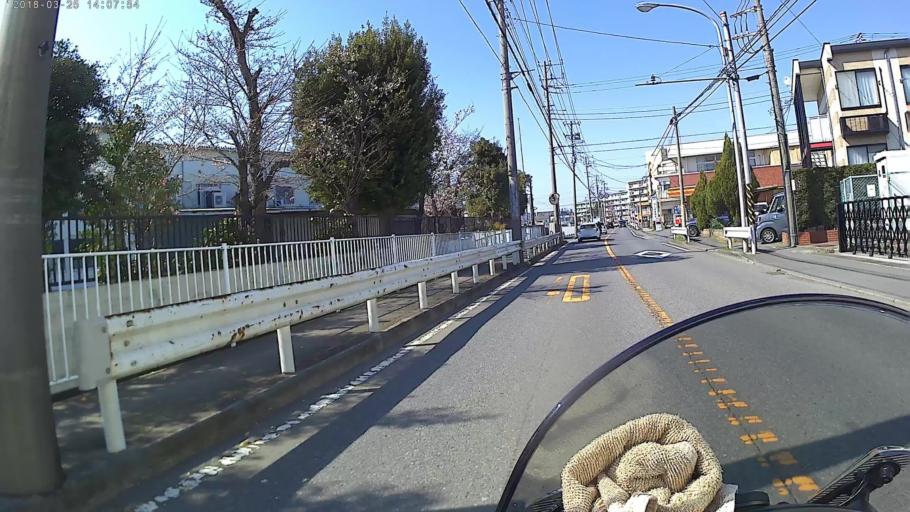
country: JP
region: Kanagawa
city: Minami-rinkan
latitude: 35.4184
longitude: 139.4796
